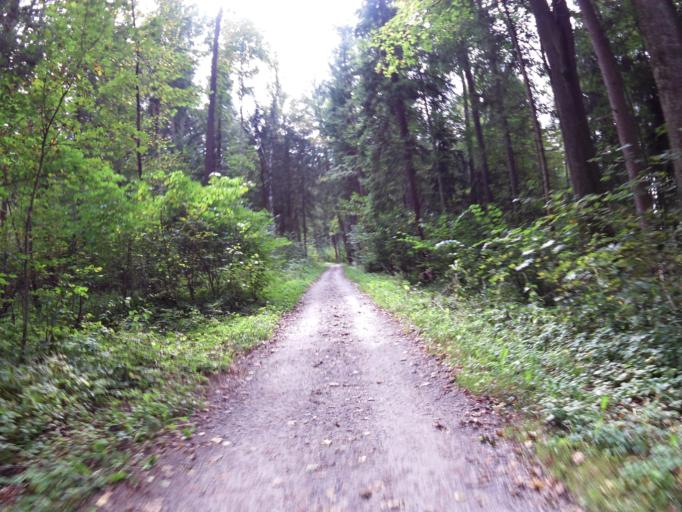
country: DE
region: Bavaria
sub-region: Upper Bavaria
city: Seeshaupt
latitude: 47.8331
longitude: 11.3380
